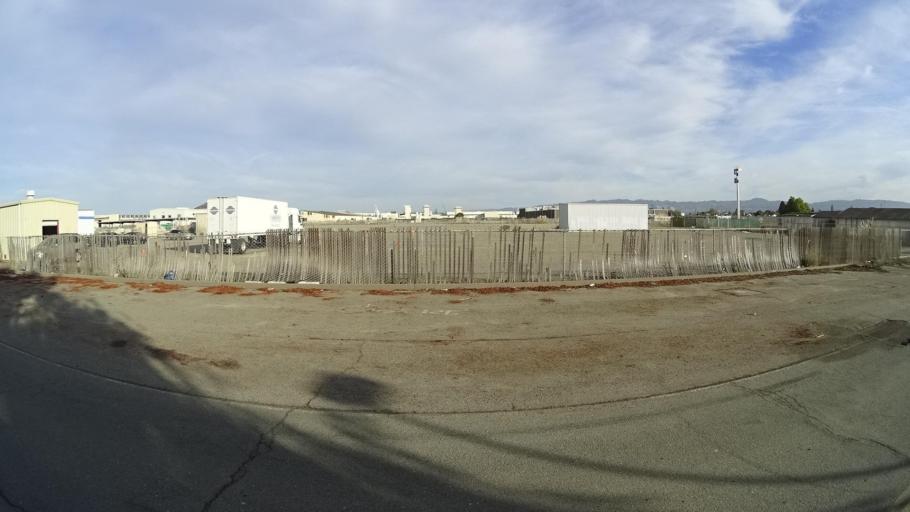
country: US
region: California
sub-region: Alameda County
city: Oakland
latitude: 37.7721
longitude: -122.2946
